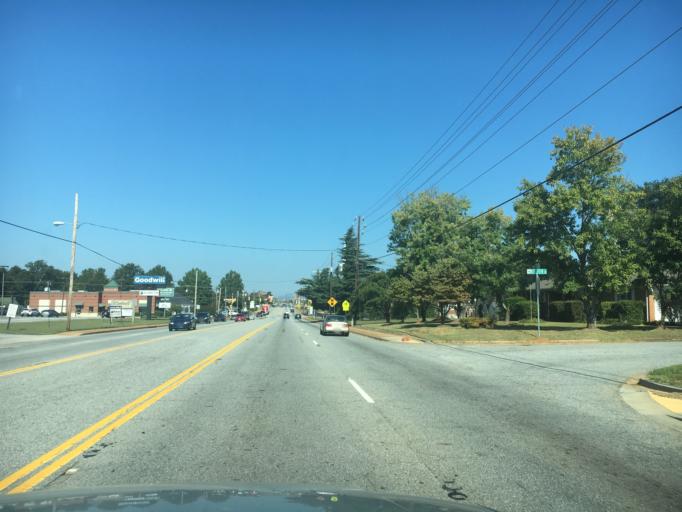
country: US
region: South Carolina
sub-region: Spartanburg County
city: Boiling Springs
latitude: 35.0428
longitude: -81.9782
